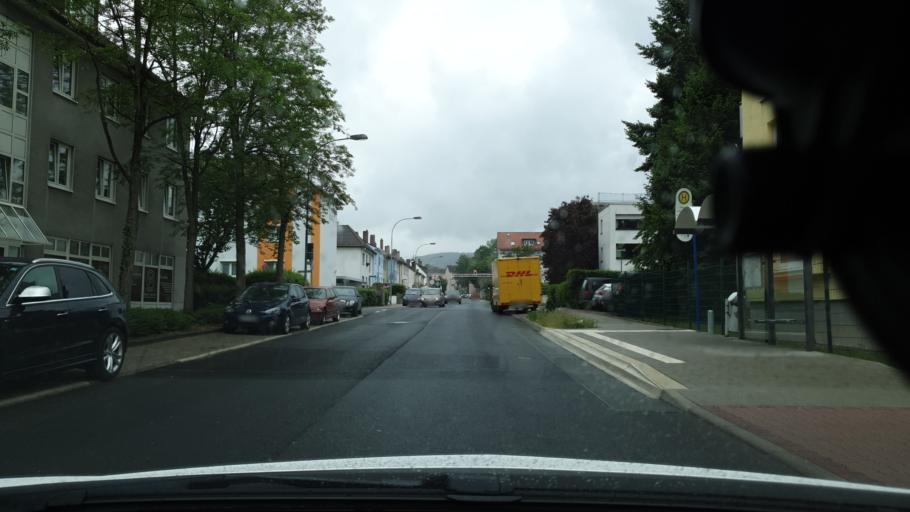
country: DE
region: Hesse
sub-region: Regierungsbezirk Darmstadt
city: Oberursel
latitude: 50.2145
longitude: 8.5664
